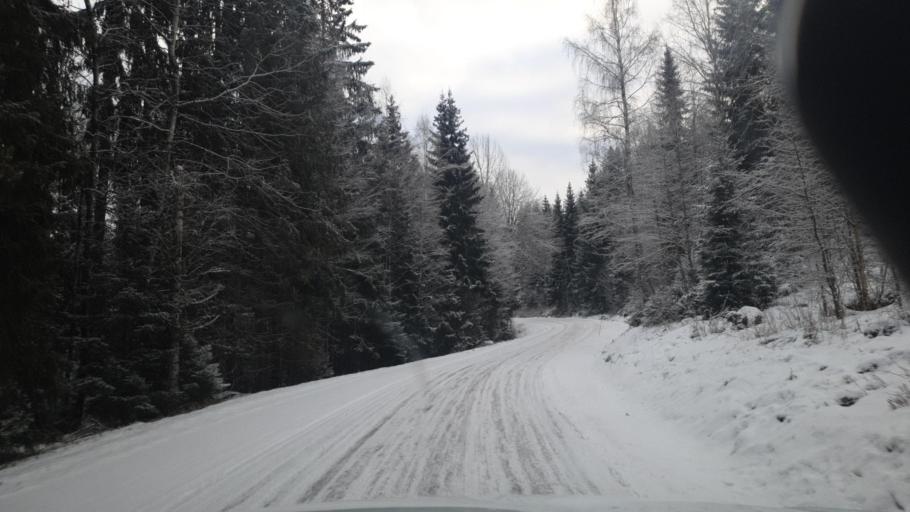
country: NO
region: Ostfold
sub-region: Romskog
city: Romskog
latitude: 59.8274
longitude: 11.9644
